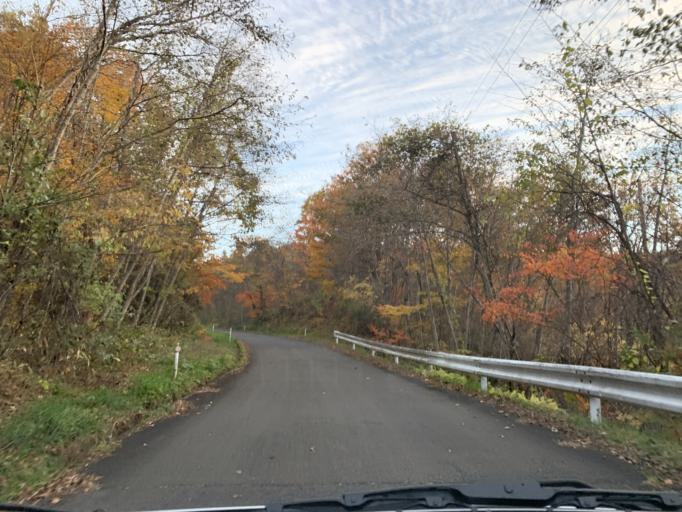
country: JP
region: Iwate
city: Ichinoseki
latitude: 38.9946
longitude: 141.0054
